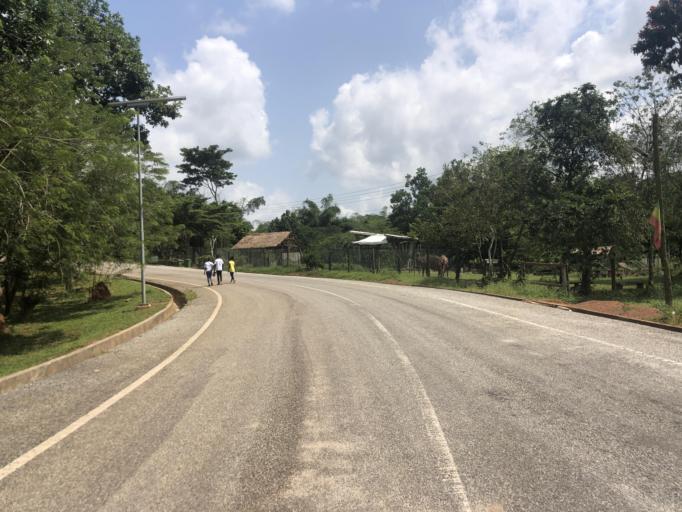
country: GH
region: Central
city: Elmina
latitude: 5.3465
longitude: -1.3836
